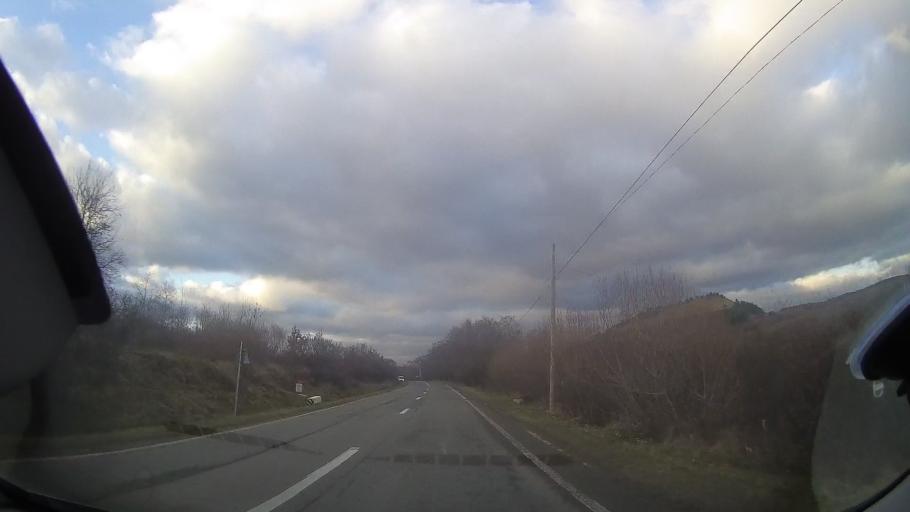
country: RO
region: Cluj
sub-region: Comuna Calatele
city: Calatele
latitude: 46.7834
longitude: 23.0046
